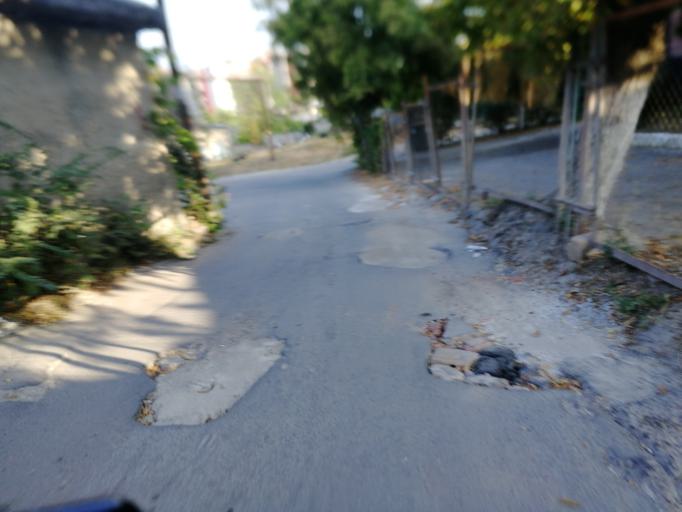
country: MD
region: Chisinau
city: Chisinau
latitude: 47.0295
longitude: 28.8687
